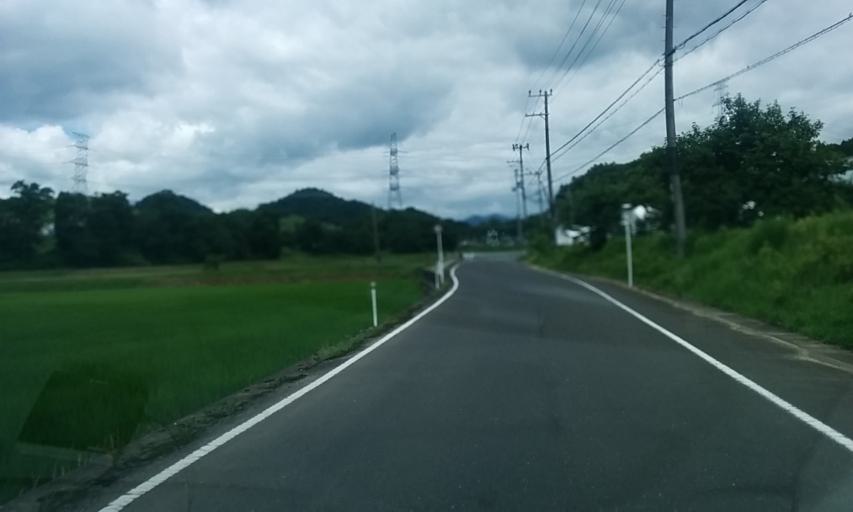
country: JP
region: Kyoto
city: Ayabe
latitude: 35.3231
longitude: 135.2722
